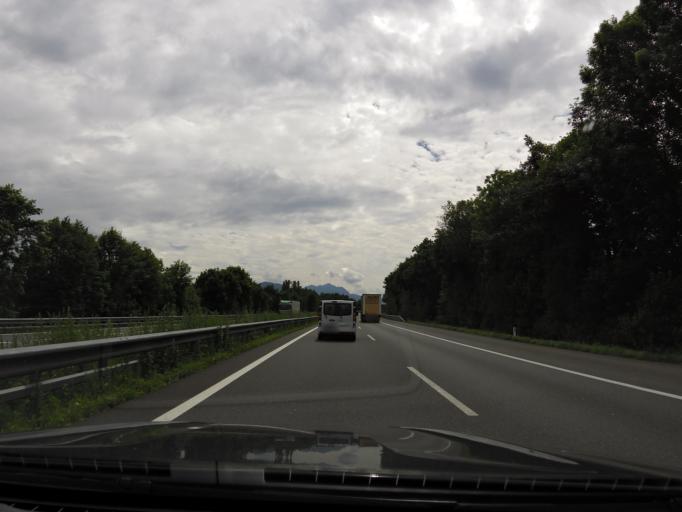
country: AT
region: Tyrol
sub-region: Politischer Bezirk Kufstein
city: Langkampfen
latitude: 47.5401
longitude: 12.1121
